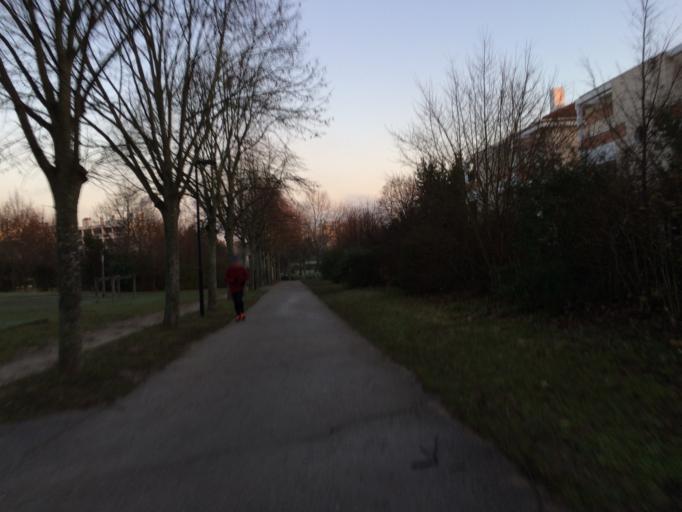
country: FR
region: Ile-de-France
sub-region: Departement des Hauts-de-Seine
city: Fontenay-aux-Roses
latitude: 48.7926
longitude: 2.2929
